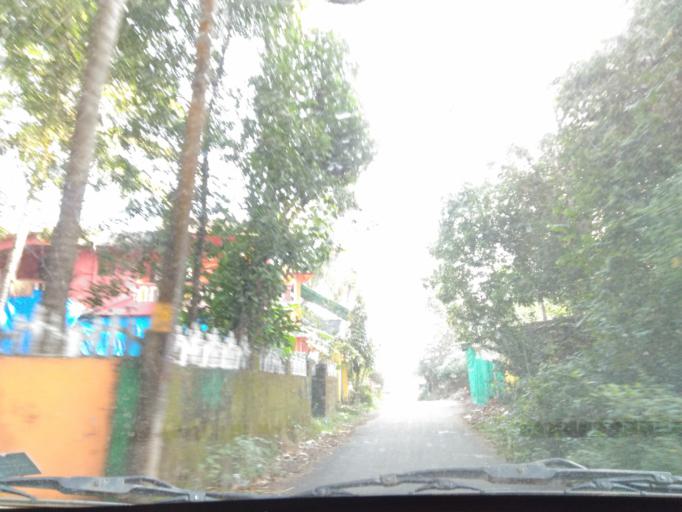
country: IN
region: Goa
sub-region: South Goa
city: Chinchinim
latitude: 15.2136
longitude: 73.9715
